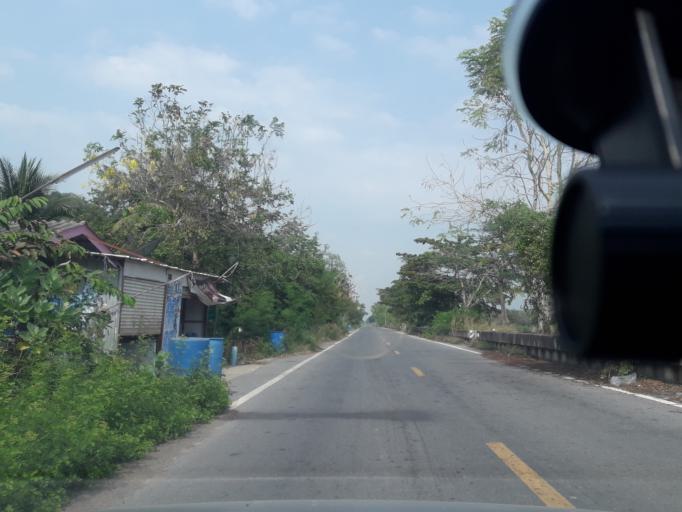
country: TH
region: Pathum Thani
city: Nong Suea
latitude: 14.1984
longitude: 100.8915
